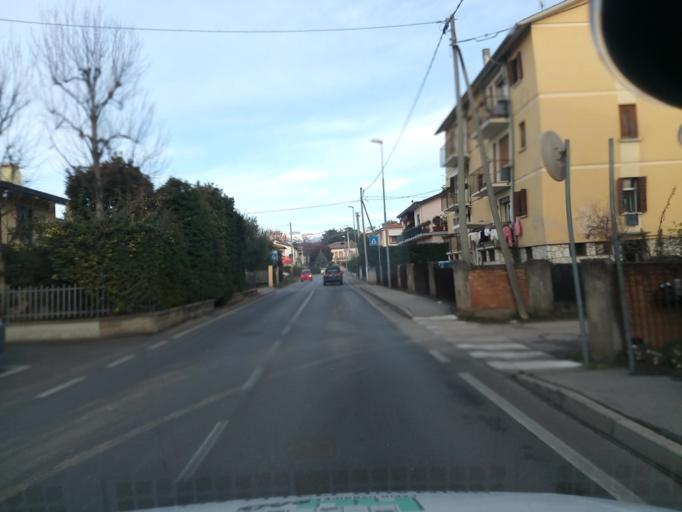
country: IT
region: Veneto
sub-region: Provincia di Treviso
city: Montebelluna
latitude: 45.7736
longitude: 12.0286
